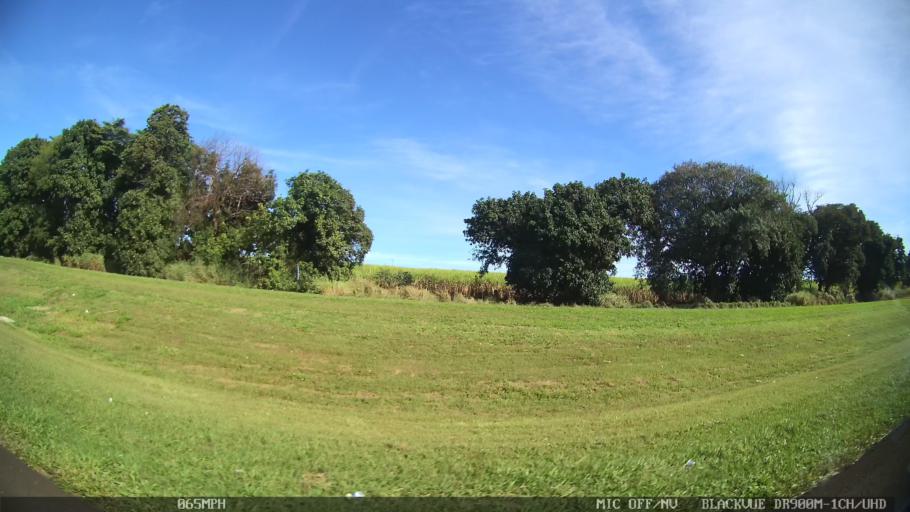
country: BR
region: Sao Paulo
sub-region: Araras
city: Araras
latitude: -22.3276
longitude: -47.3895
